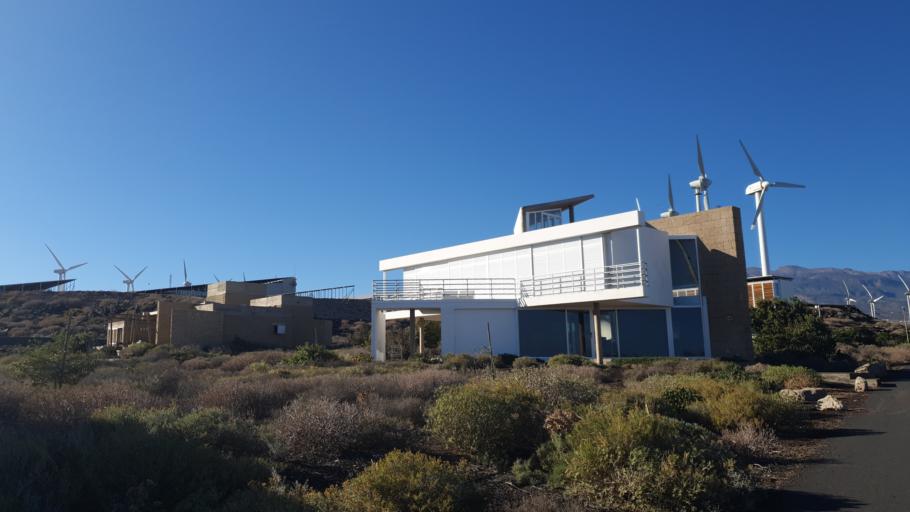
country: ES
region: Canary Islands
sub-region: Provincia de Santa Cruz de Tenerife
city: San Isidro
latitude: 28.0686
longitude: -16.5088
